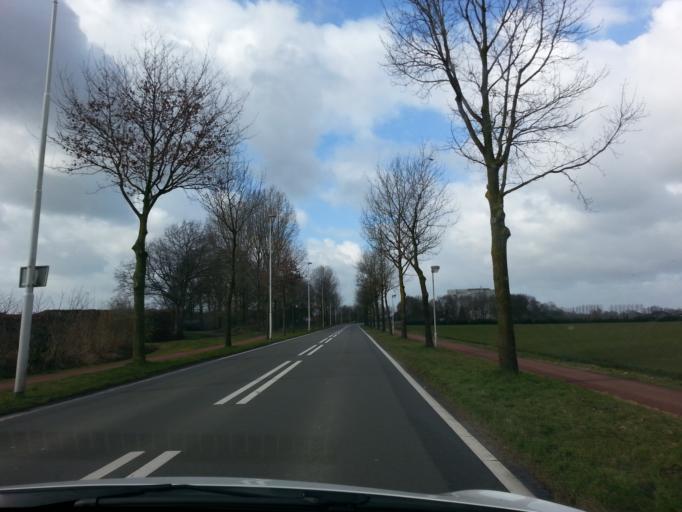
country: NL
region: North Brabant
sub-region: Gemeente Best
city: Best
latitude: 51.5061
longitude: 5.3577
